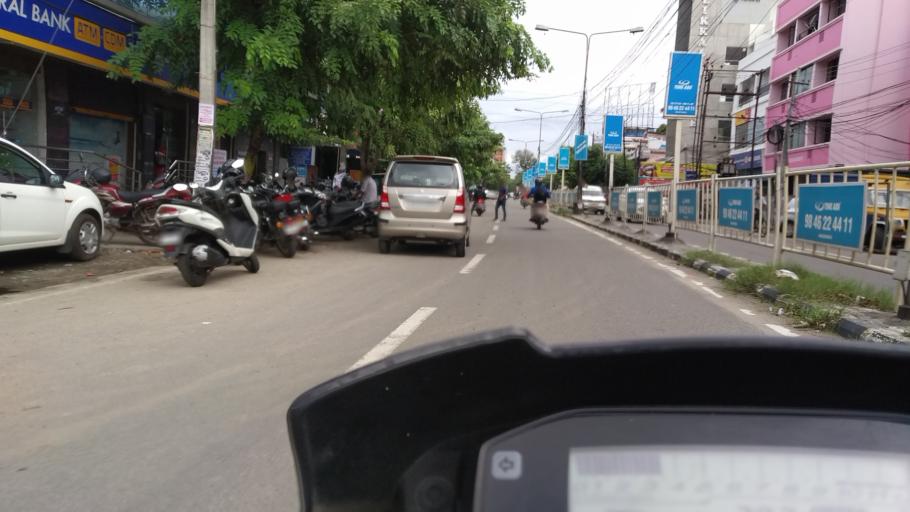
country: IN
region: Kerala
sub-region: Ernakulam
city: Cochin
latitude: 9.9927
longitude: 76.2927
